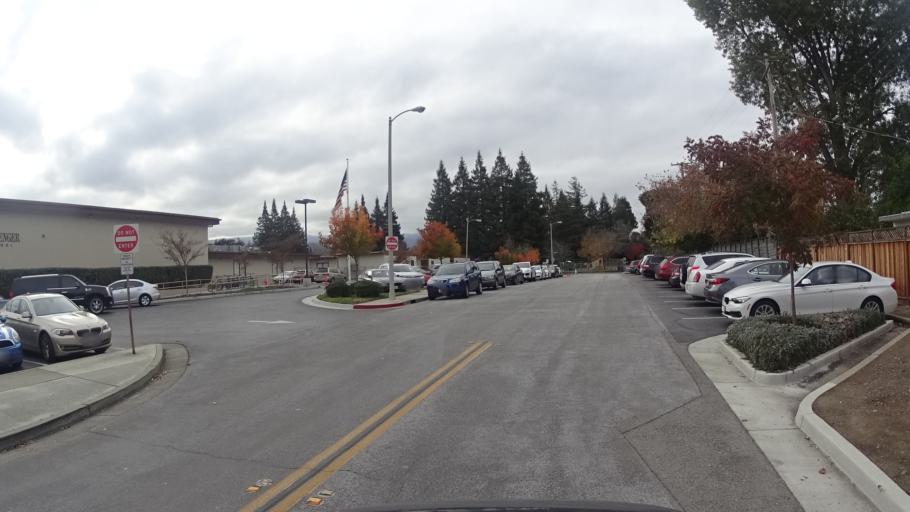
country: US
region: California
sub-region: Santa Clara County
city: Sunnyvale
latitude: 37.3558
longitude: -122.0417
